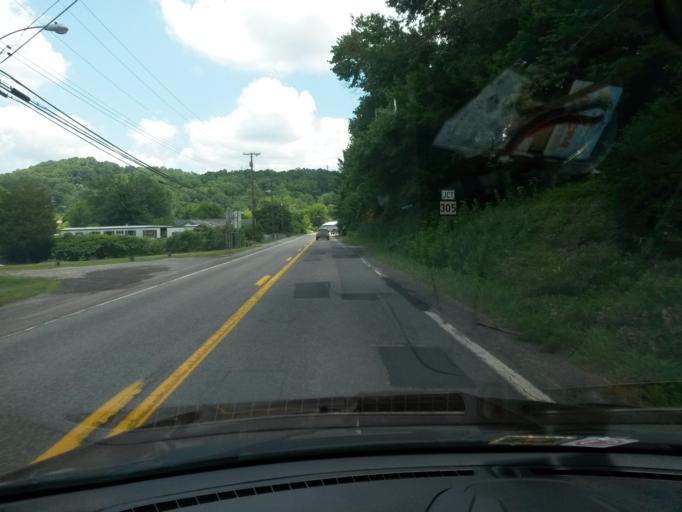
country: US
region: West Virginia
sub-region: Raleigh County
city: Sophia
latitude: 37.7329
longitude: -81.3007
